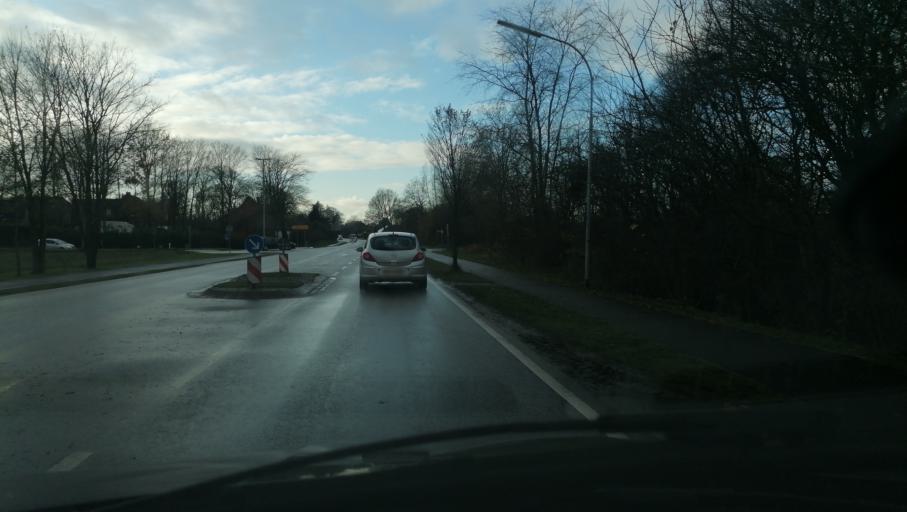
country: DE
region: Schleswig-Holstein
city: Nindorf
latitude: 54.0878
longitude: 9.1236
